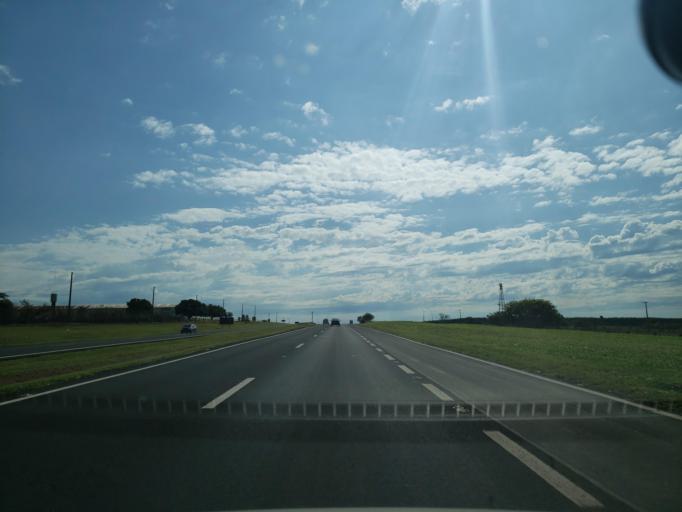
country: BR
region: Sao Paulo
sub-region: Pirajui
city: Pirajui
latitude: -22.0069
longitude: -49.4247
